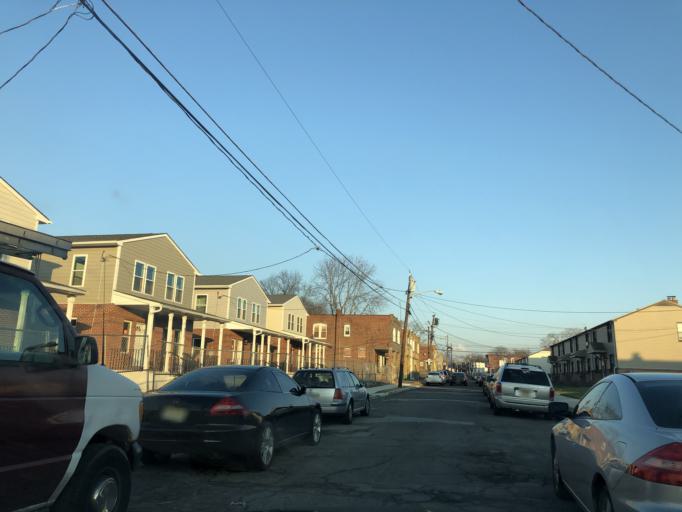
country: US
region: New Jersey
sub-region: Camden County
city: Camden
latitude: 39.9246
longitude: -75.1103
